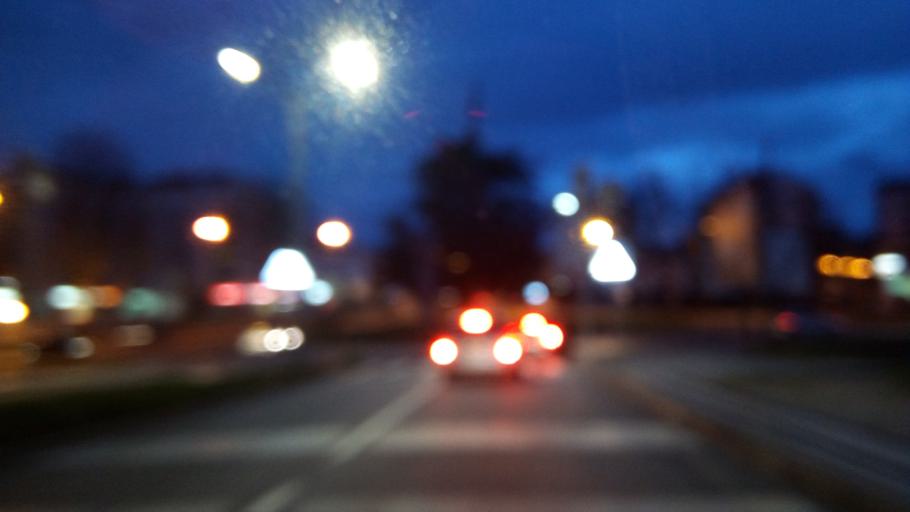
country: PT
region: Viseu
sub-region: Viseu
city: Viseu
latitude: 40.6499
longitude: -7.9125
